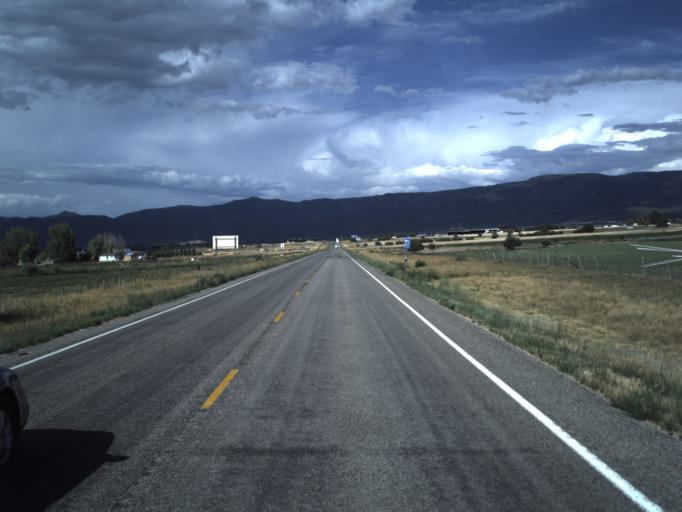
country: US
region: Utah
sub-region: Sanpete County
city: Mount Pleasant
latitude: 39.5152
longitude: -111.4899
